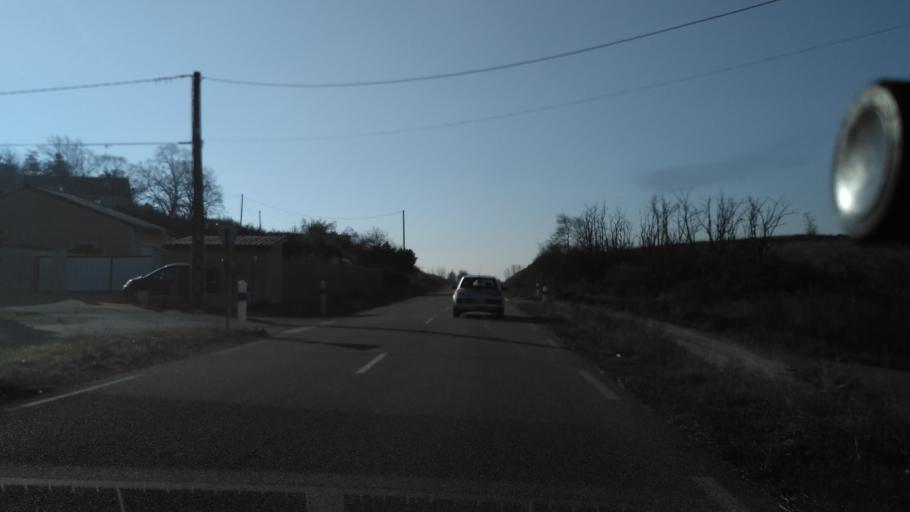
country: FR
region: Rhone-Alpes
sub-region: Departement de la Drome
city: Genissieux
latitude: 45.1004
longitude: 5.0940
